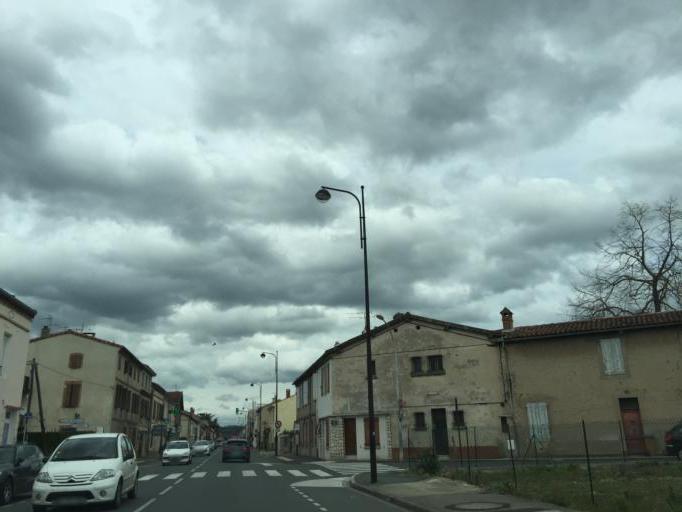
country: FR
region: Midi-Pyrenees
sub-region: Departement du Tarn
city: Albi
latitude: 43.9382
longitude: 2.1476
